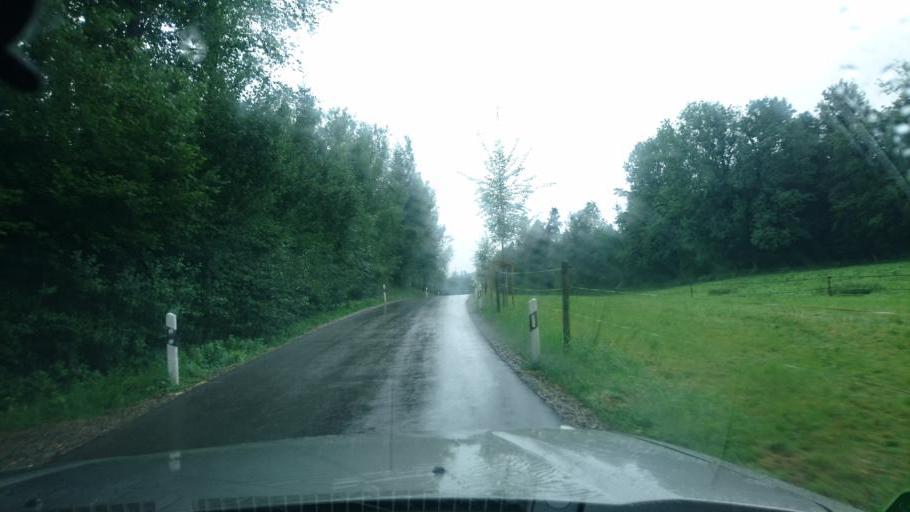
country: CH
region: Zurich
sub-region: Bezirk Hinwil
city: Gossau
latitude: 47.3132
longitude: 8.7460
